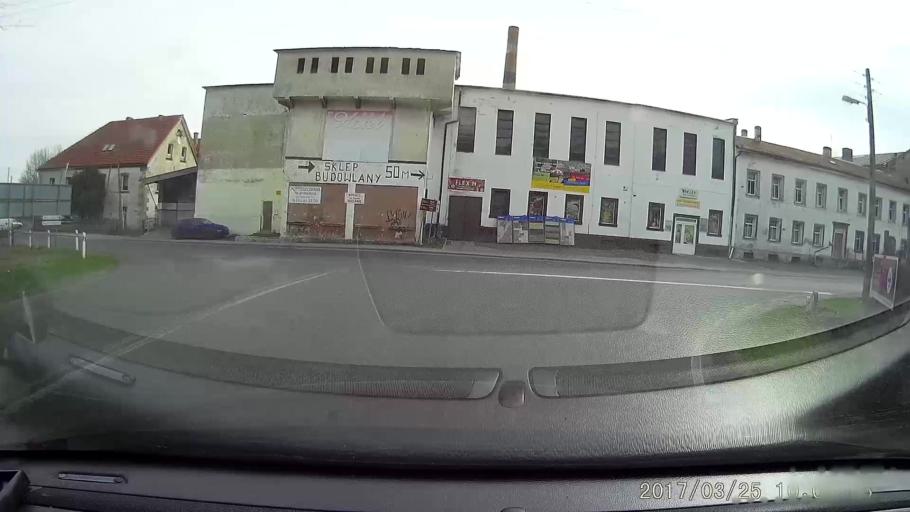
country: PL
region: Lower Silesian Voivodeship
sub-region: Powiat lubanski
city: Swieradow-Zdroj
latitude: 50.9308
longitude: 15.3546
